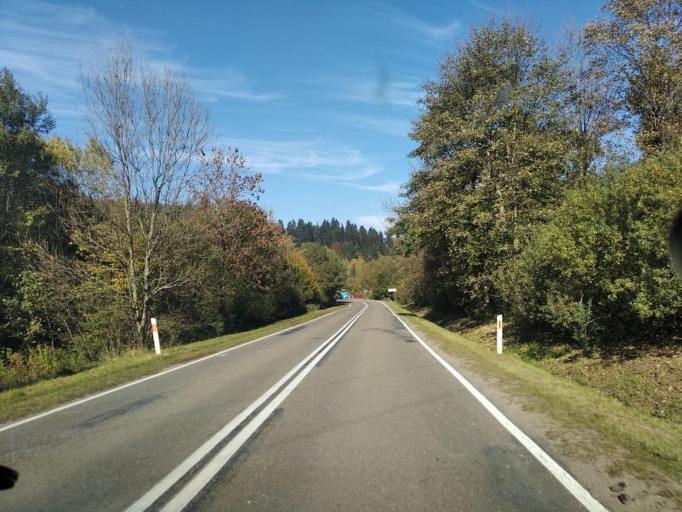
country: PL
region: Subcarpathian Voivodeship
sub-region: Powiat leski
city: Baligrod
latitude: 49.3213
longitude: 22.2775
